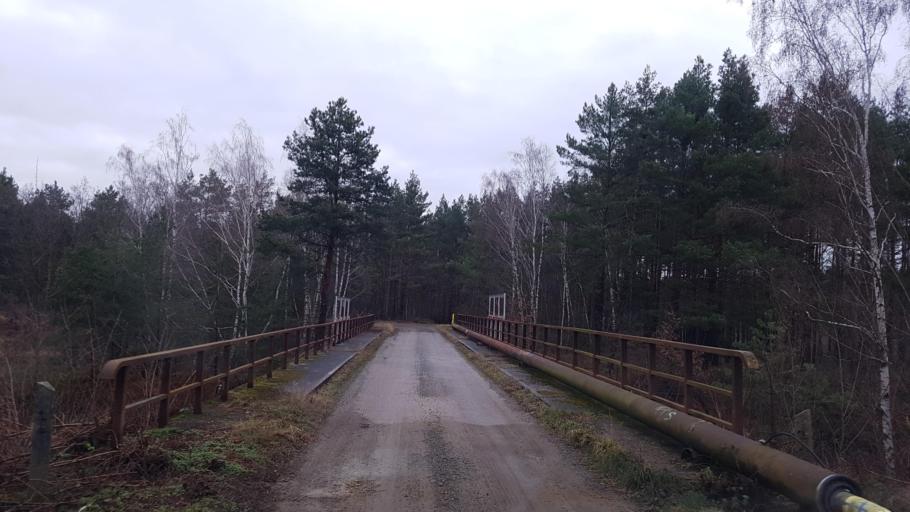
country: DE
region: Brandenburg
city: Altdobern
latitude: 51.6443
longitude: 14.0047
